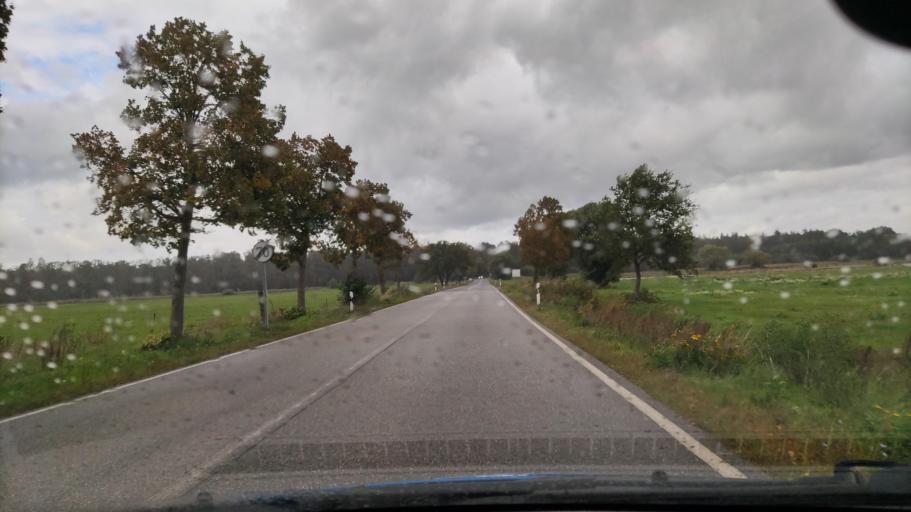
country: DE
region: Brandenburg
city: Lanz
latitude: 52.9952
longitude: 11.5488
